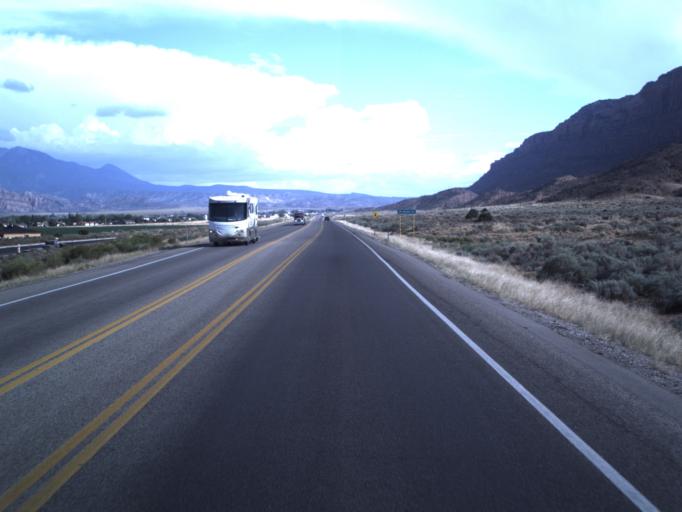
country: US
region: Utah
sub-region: Grand County
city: Moab
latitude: 38.5144
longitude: -109.4897
